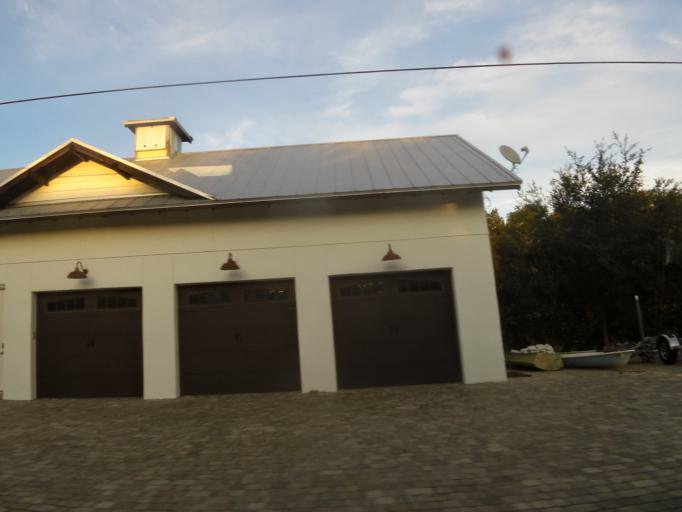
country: US
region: Florida
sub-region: Saint Johns County
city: Palm Valley
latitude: 30.1305
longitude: -81.3829
